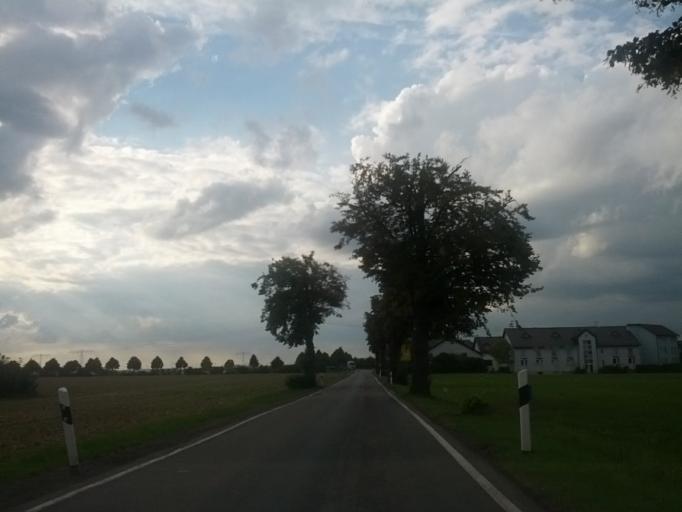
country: DE
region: Thuringia
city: Schwabhausen
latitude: 50.9208
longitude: 10.7317
